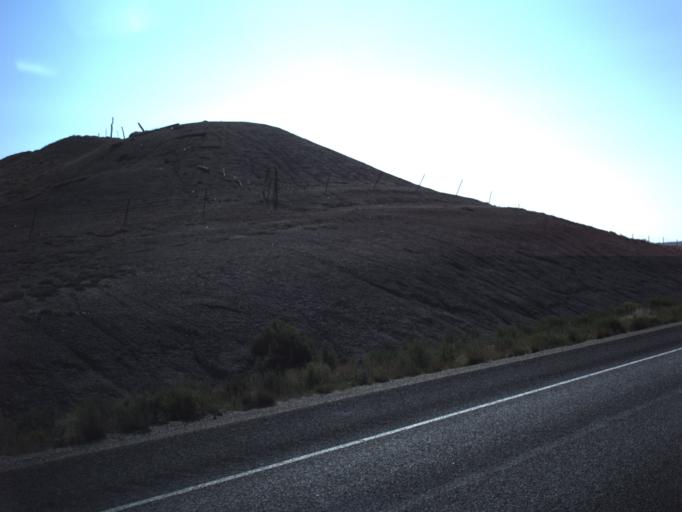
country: US
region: Utah
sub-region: Emery County
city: Ferron
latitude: 39.0589
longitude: -111.1283
